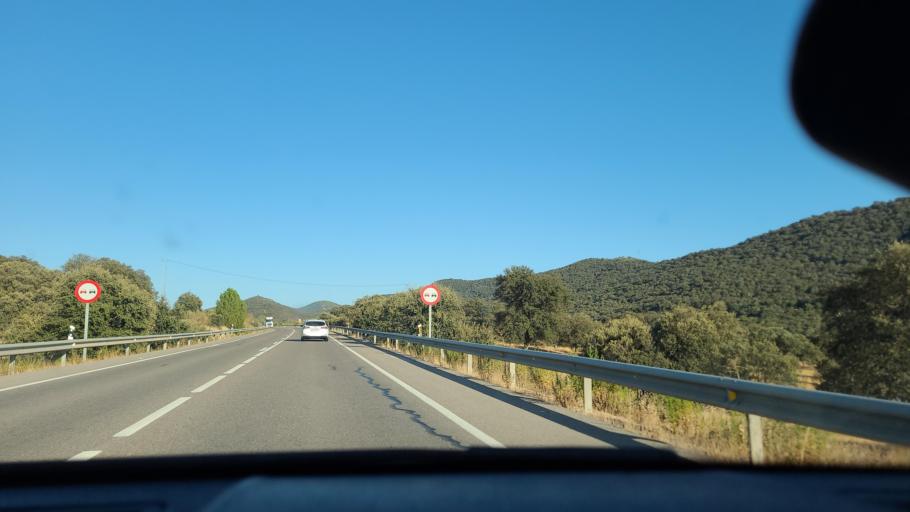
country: ES
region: Andalusia
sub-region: Province of Cordoba
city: Villaharta
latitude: 38.1319
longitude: -4.9374
